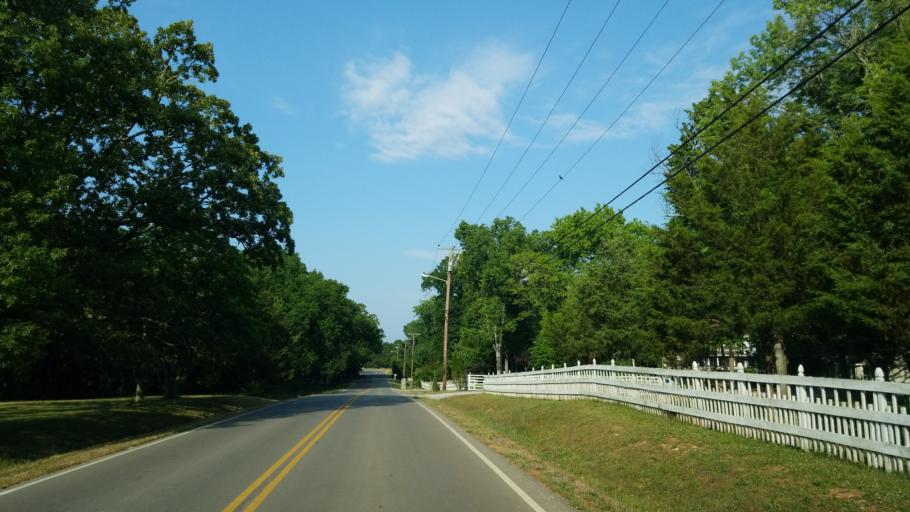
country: US
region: Tennessee
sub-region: Rutherford County
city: La Vergne
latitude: 36.0423
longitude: -86.5891
